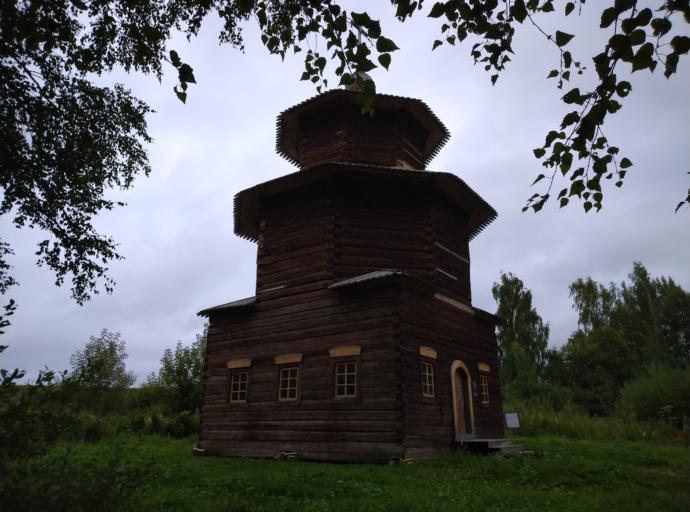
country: RU
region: Kostroma
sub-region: Kostromskoy Rayon
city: Kostroma
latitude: 57.7733
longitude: 40.8923
